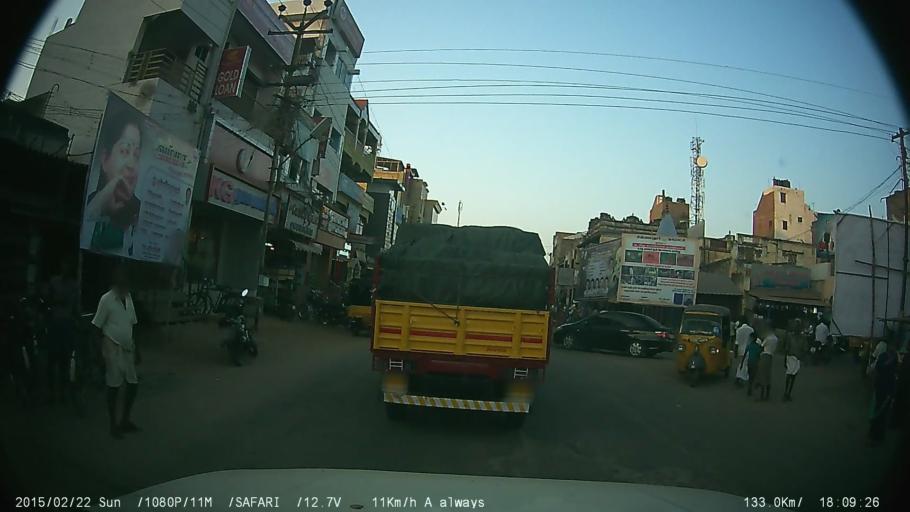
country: IN
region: Tamil Nadu
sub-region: Theni
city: Chinnamanur
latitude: 9.8408
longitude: 77.3794
